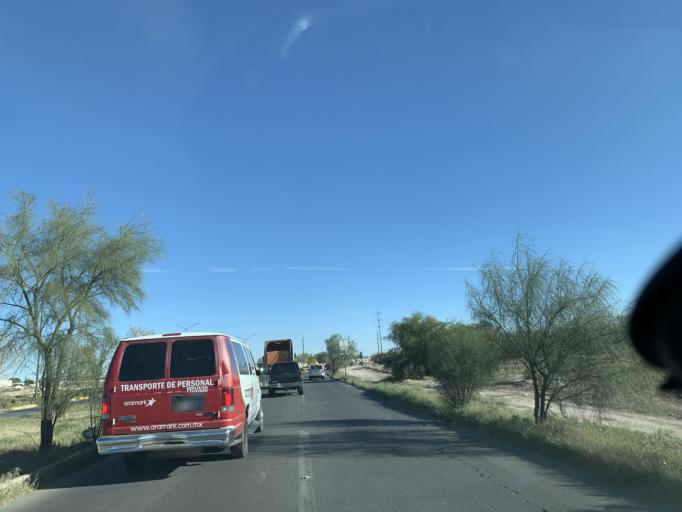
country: US
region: Texas
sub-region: El Paso County
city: Socorro
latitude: 31.7061
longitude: -106.3814
